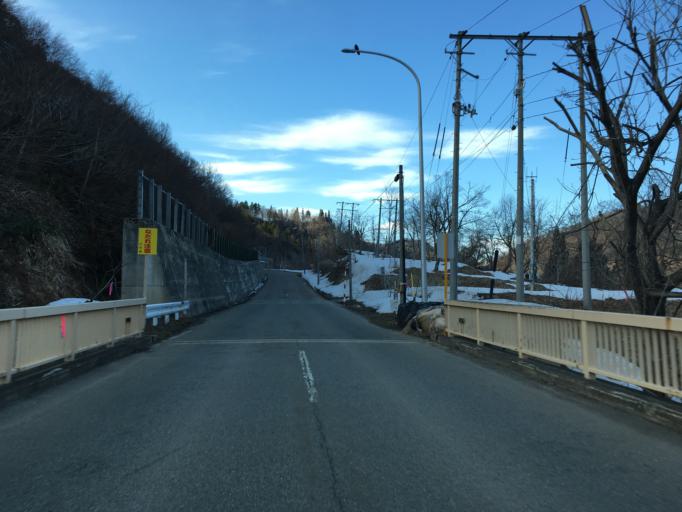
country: JP
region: Yamagata
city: Nagai
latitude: 37.9517
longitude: 139.9176
